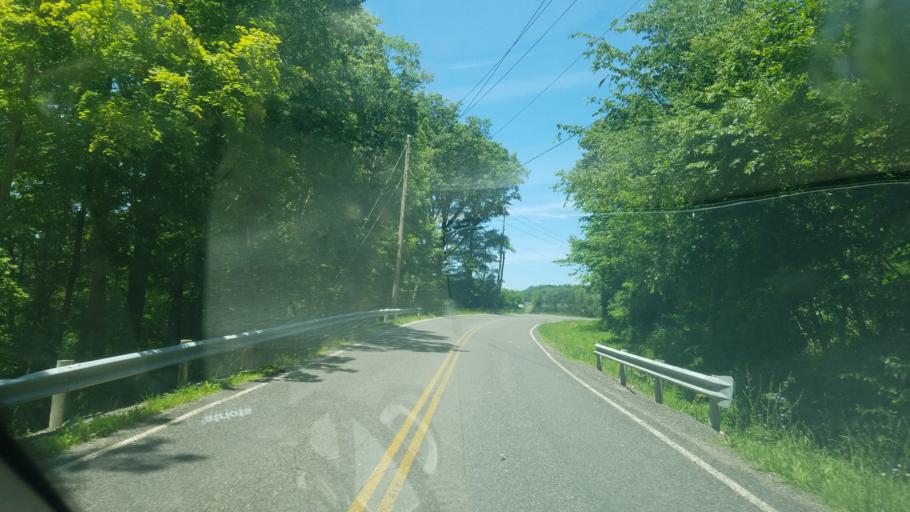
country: US
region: Ohio
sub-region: Columbiana County
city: Glenmoor
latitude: 40.7411
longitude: -80.6437
